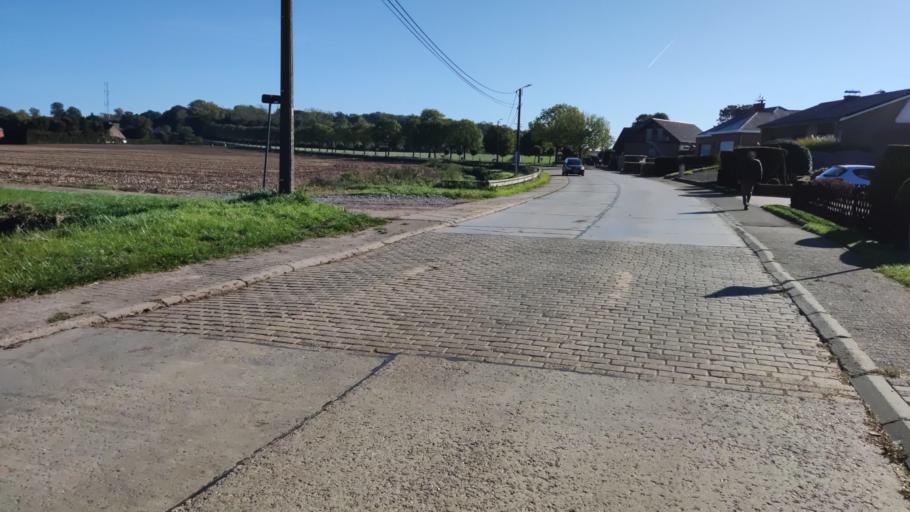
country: BE
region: Flanders
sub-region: Provincie Vlaams-Brabant
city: Zoutleeuw
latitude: 50.8137
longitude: 5.0248
